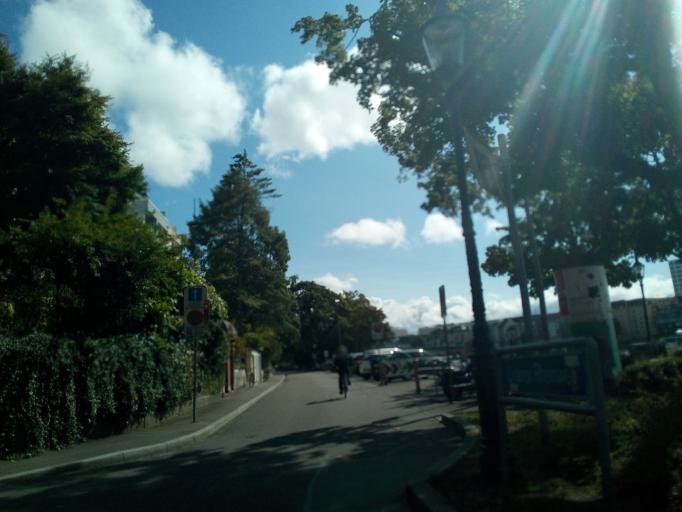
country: CH
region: Basel-City
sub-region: Basel-Stadt
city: Basel
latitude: 47.5693
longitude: 7.5865
